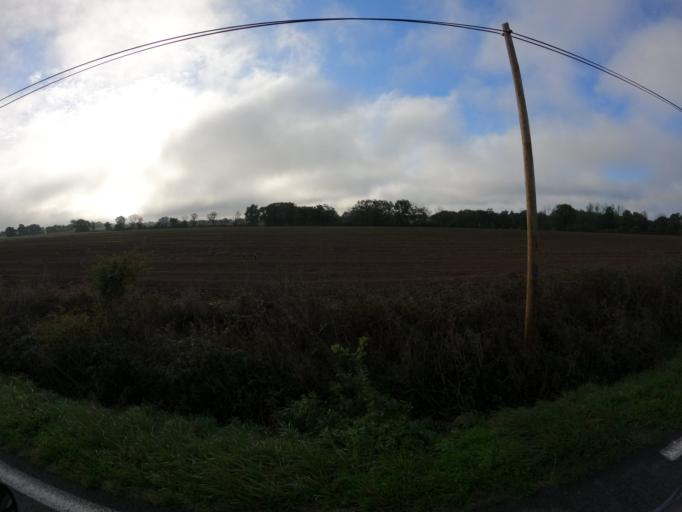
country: FR
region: Pays de la Loire
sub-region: Departement de la Vendee
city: La Bruffiere
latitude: 46.9899
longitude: -1.1891
